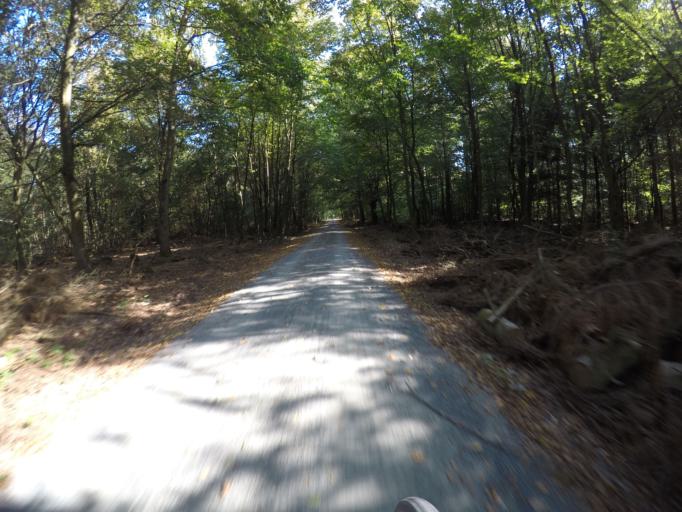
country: DE
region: Hesse
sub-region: Regierungsbezirk Darmstadt
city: Neu Isenburg
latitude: 50.0436
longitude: 8.6574
